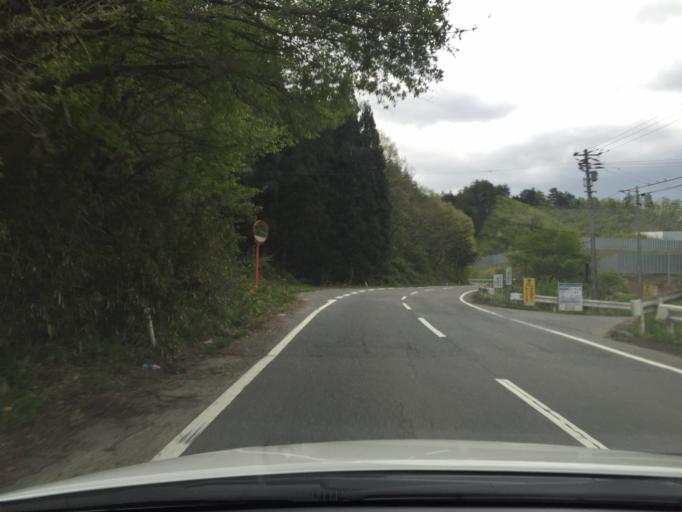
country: JP
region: Fukushima
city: Yanagawamachi-saiwaicho
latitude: 37.7535
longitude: 140.6908
